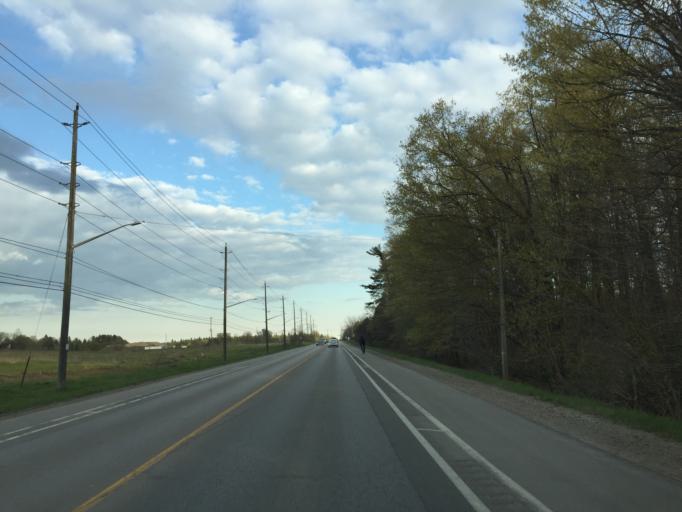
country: CA
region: Ontario
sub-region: Wellington County
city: Guelph
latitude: 43.5437
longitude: -80.2125
